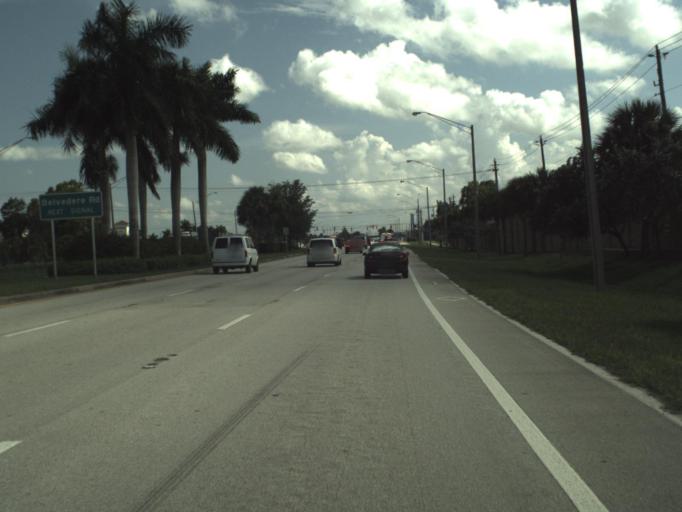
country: US
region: Florida
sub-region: Palm Beach County
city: Royal Palm Beach
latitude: 26.6949
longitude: -80.2016
